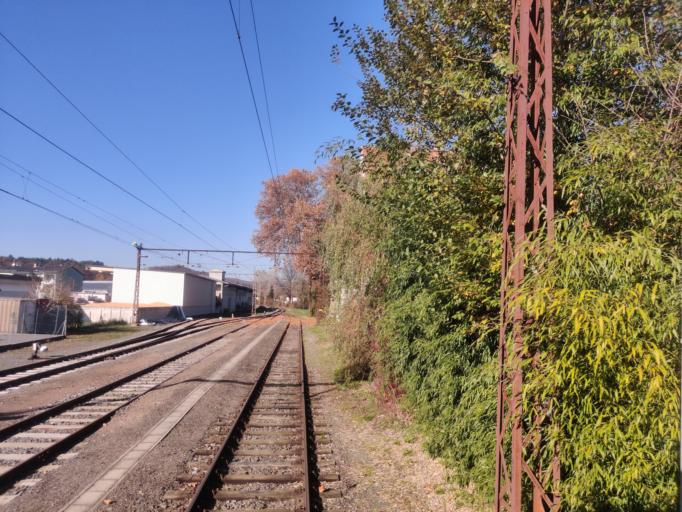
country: AT
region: Styria
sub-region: Politischer Bezirk Suedoststeiermark
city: Bad Gleichenberg
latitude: 46.8720
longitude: 15.9032
